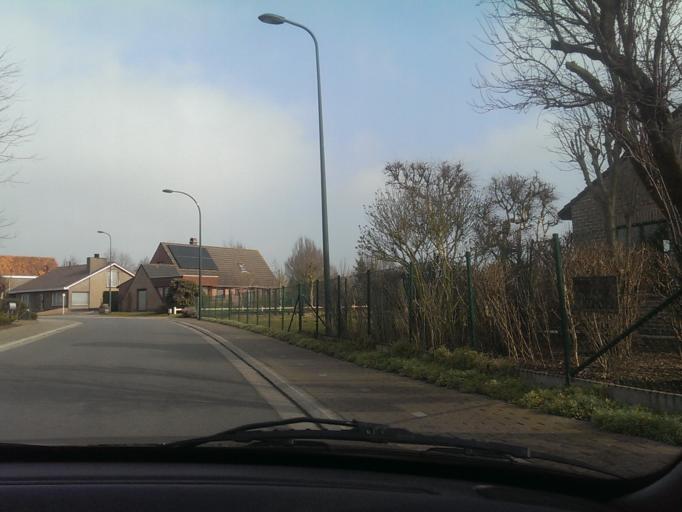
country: BE
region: Flanders
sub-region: Provincie West-Vlaanderen
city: Roeselare
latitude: 50.9353
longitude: 3.0940
